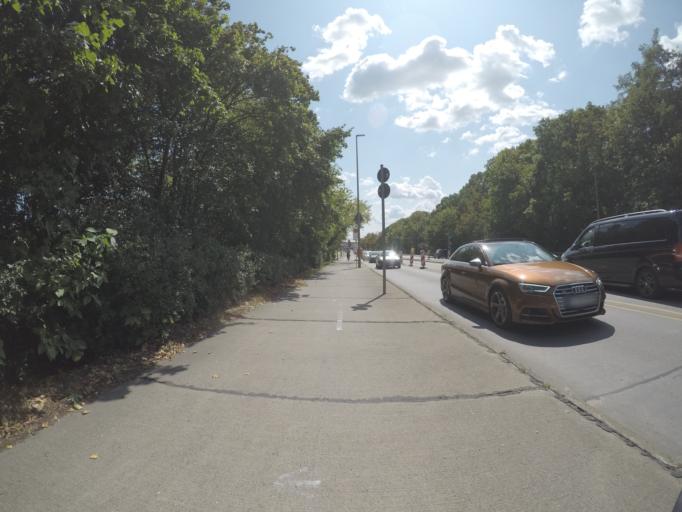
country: DE
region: Berlin
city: Biesdorf
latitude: 52.5121
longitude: 13.5625
